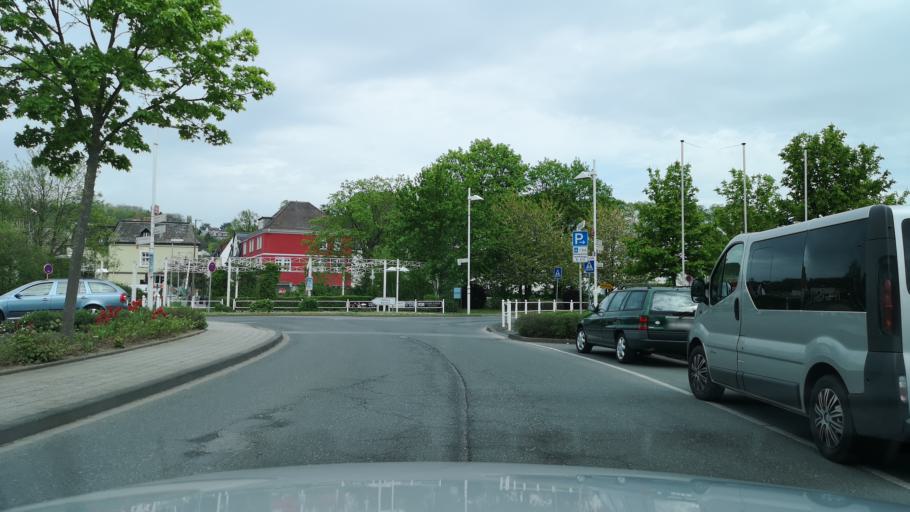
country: DE
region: North Rhine-Westphalia
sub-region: Regierungsbezirk Arnsberg
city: Frondenberg
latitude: 51.4712
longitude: 7.7685
